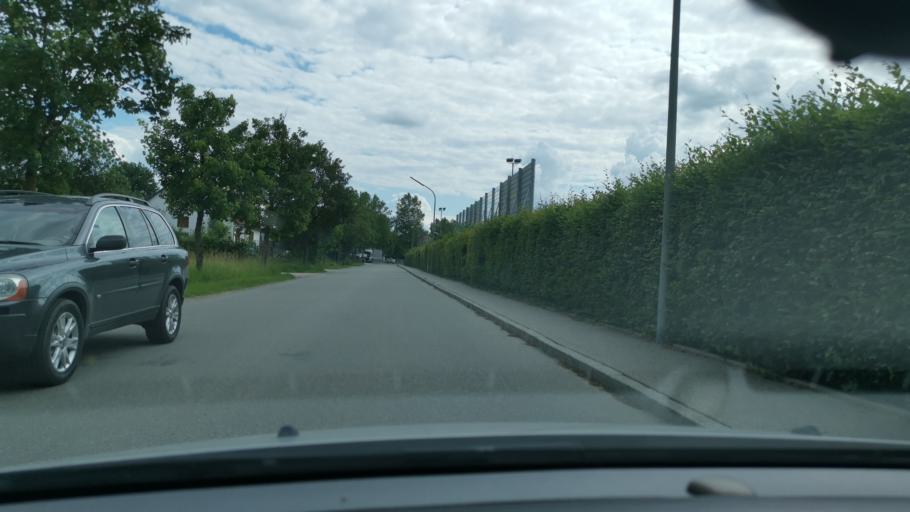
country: DE
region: Bavaria
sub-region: Upper Bavaria
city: Moosburg
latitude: 48.4792
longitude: 11.9464
